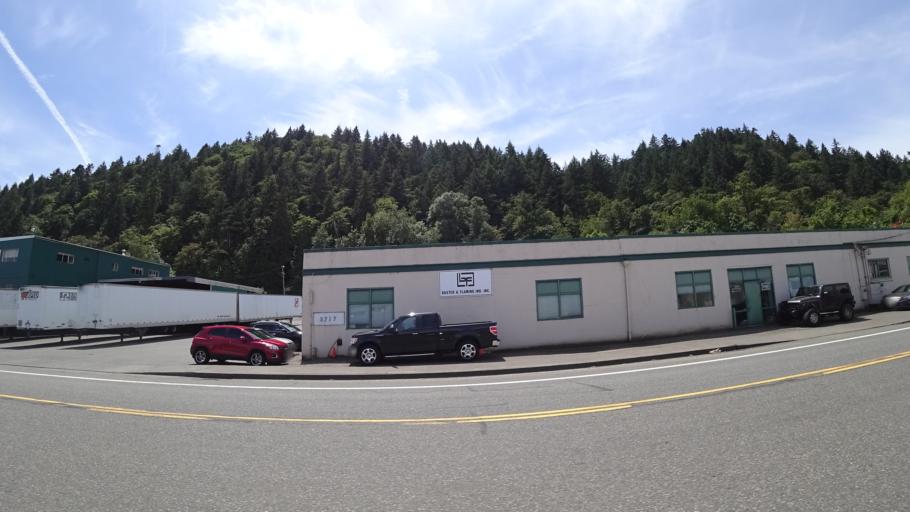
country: US
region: Oregon
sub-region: Washington County
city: West Haven-Sylvan
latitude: 45.5489
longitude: -122.7268
